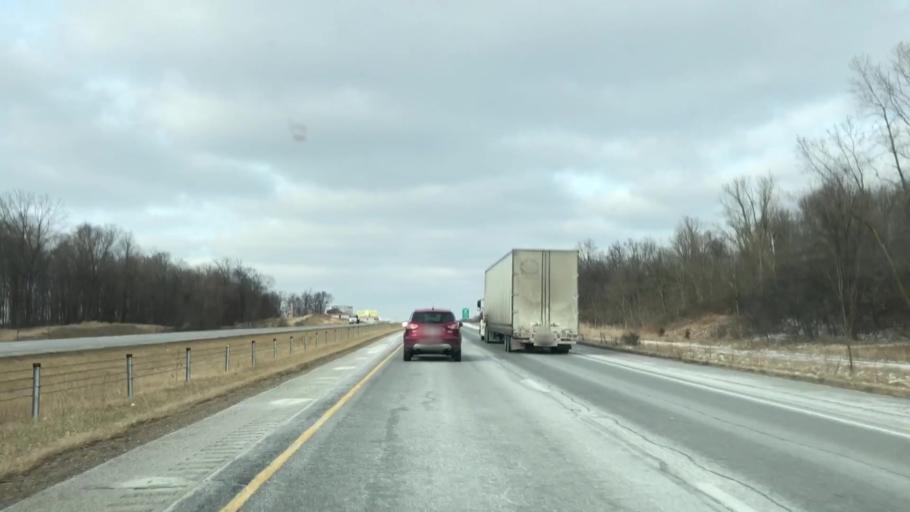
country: US
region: Indiana
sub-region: DeKalb County
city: Waterloo
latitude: 41.5053
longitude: -85.0551
